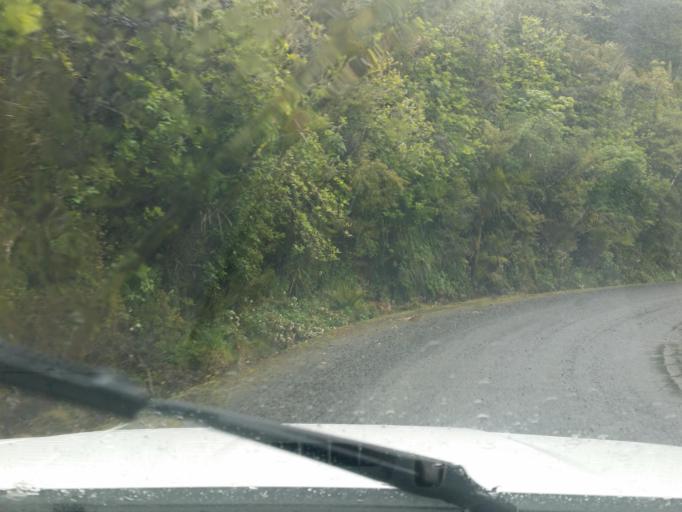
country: NZ
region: Northland
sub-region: Kaipara District
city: Dargaville
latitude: -35.7473
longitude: 173.9604
